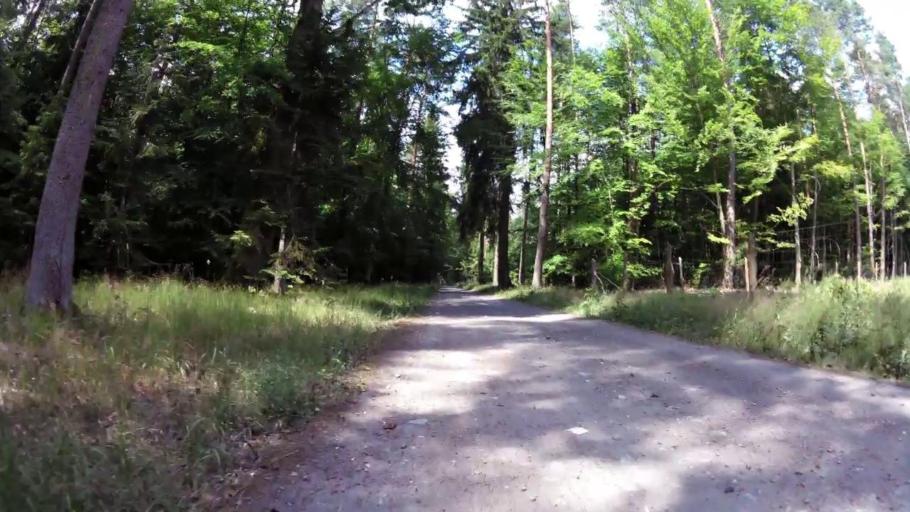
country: PL
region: West Pomeranian Voivodeship
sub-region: Powiat lobeski
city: Lobez
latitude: 53.5816
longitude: 15.6549
